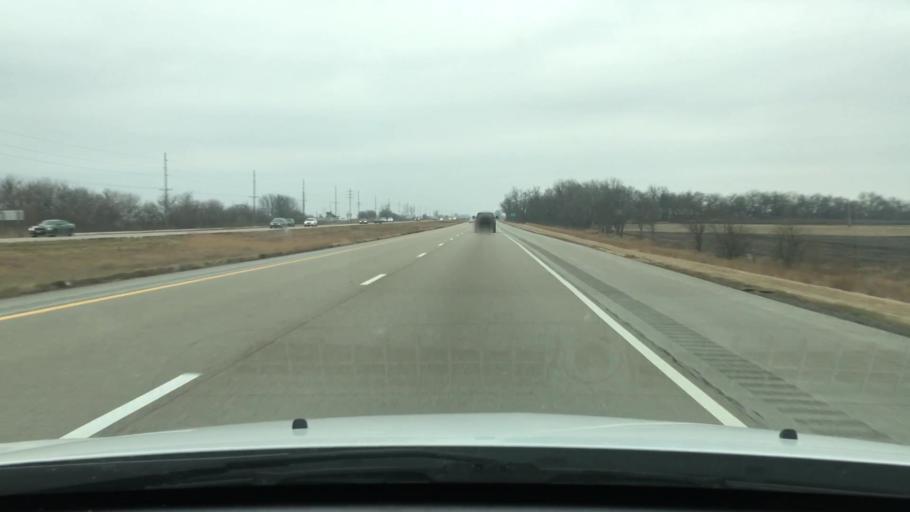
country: US
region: Illinois
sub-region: Logan County
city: Atlanta
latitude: 40.2795
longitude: -89.2092
